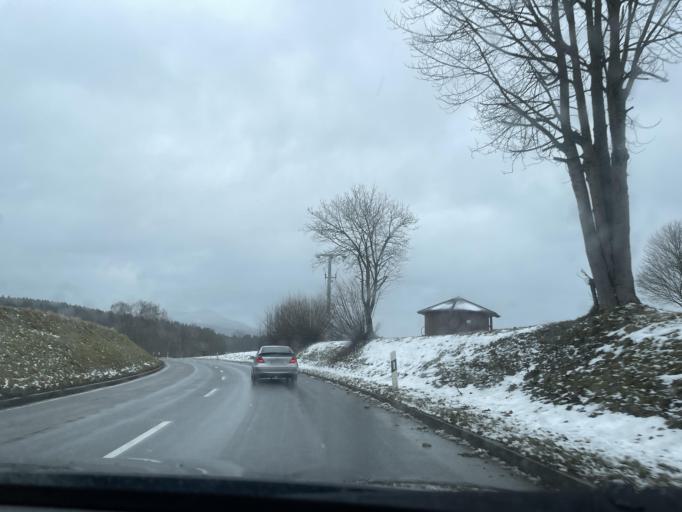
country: DE
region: Bavaria
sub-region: Upper Palatinate
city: Kotzting
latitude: 49.2100
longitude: 12.8447
